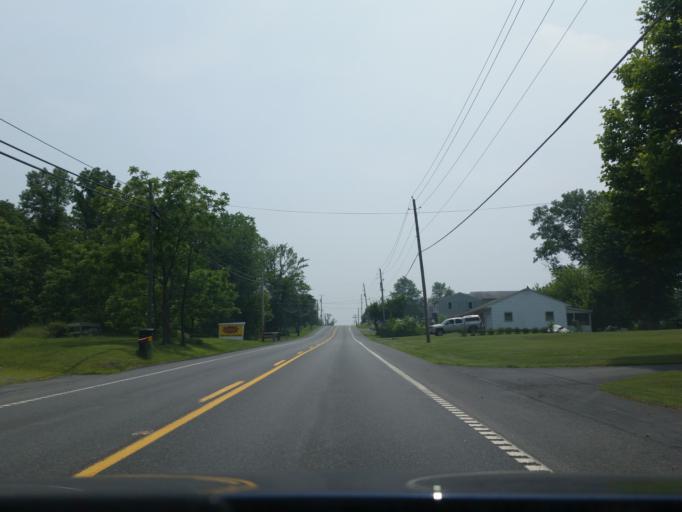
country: US
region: Pennsylvania
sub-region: Lebanon County
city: Jonestown
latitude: 40.4409
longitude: -76.5096
